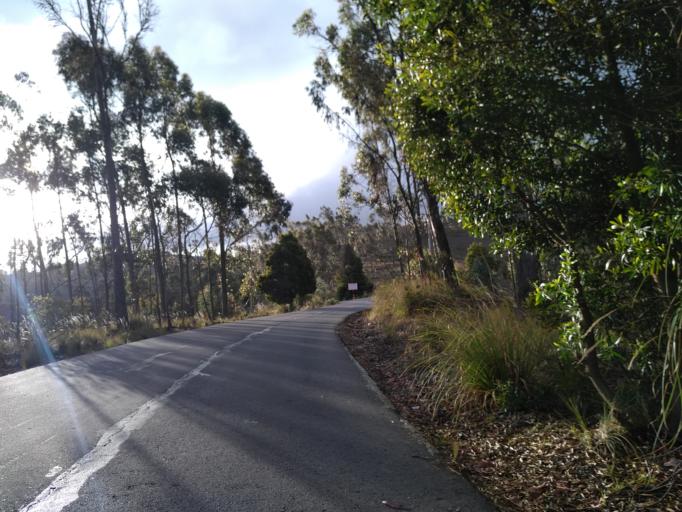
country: EC
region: Chimborazo
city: Riobamba
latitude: -1.7027
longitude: -78.7085
